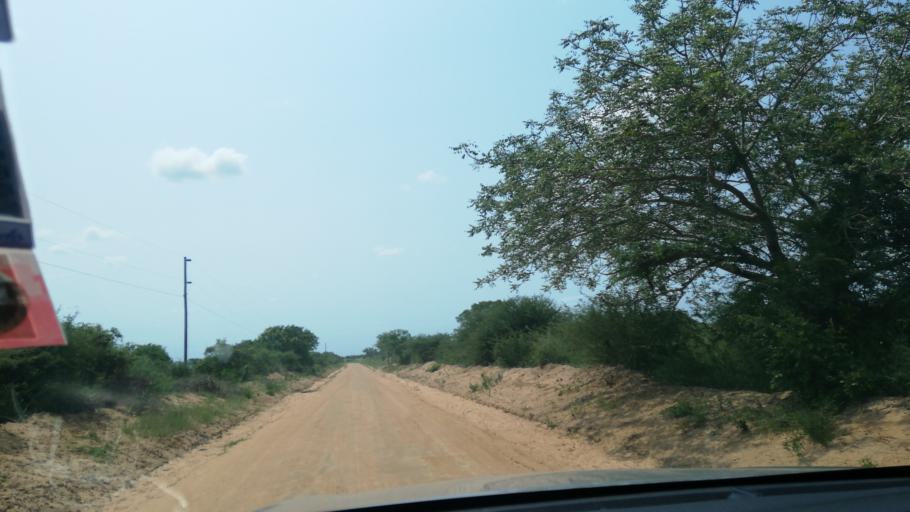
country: MZ
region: Maputo
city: Matola
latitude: -26.0909
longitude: 32.3906
